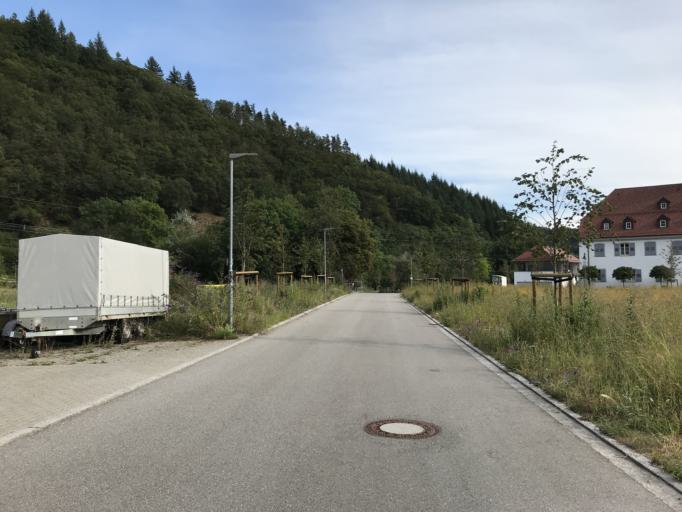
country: DE
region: Baden-Wuerttemberg
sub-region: Freiburg Region
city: Hausen
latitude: 47.6872
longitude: 7.8434
